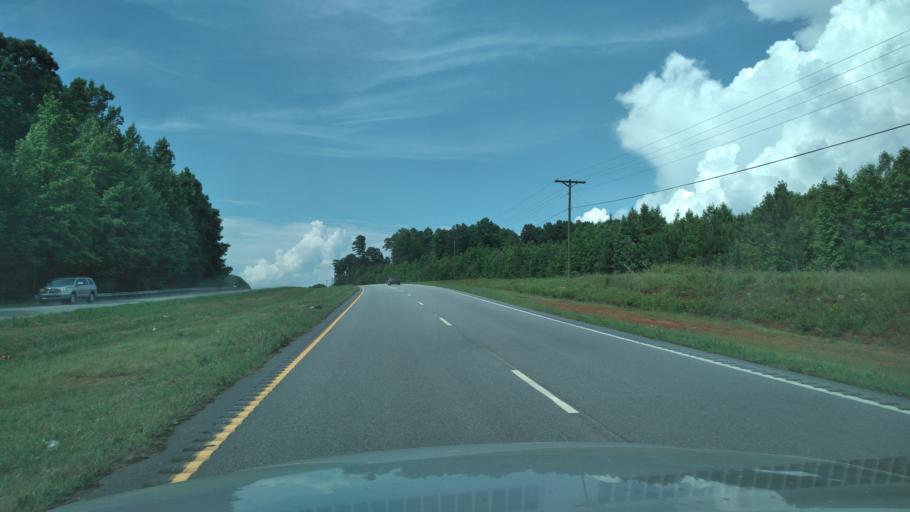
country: US
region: South Carolina
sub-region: Spartanburg County
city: Woodruff
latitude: 34.7799
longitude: -82.0247
